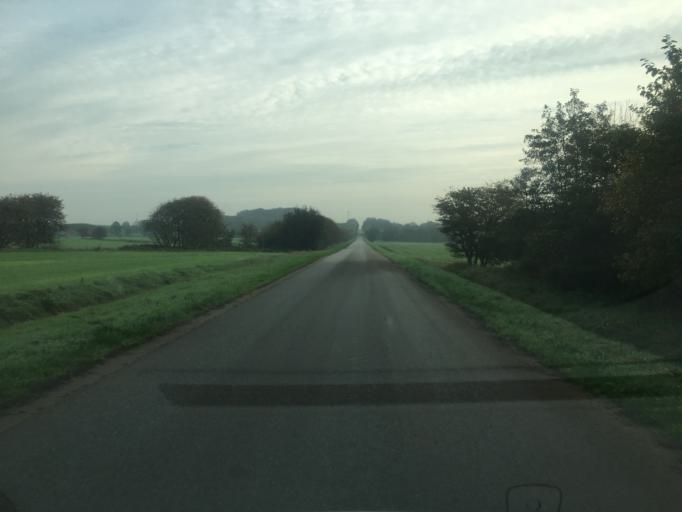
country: DK
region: South Denmark
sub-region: Tonder Kommune
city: Toftlund
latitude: 55.1030
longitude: 9.0749
